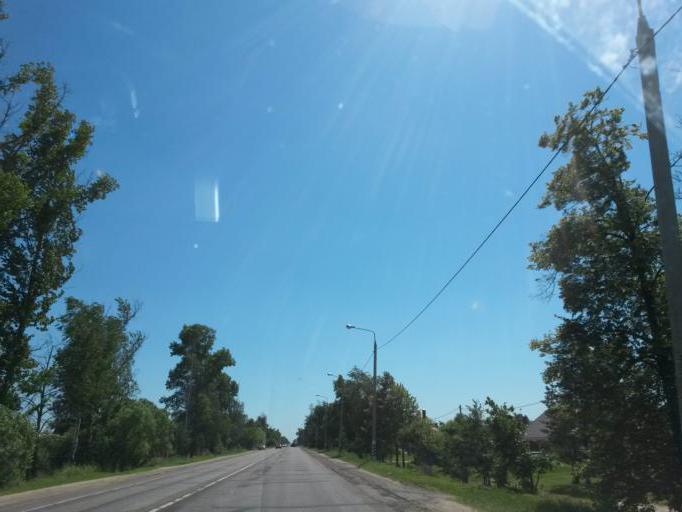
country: RU
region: Moskovskaya
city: Proletarskiy
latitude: 55.0769
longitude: 37.4389
